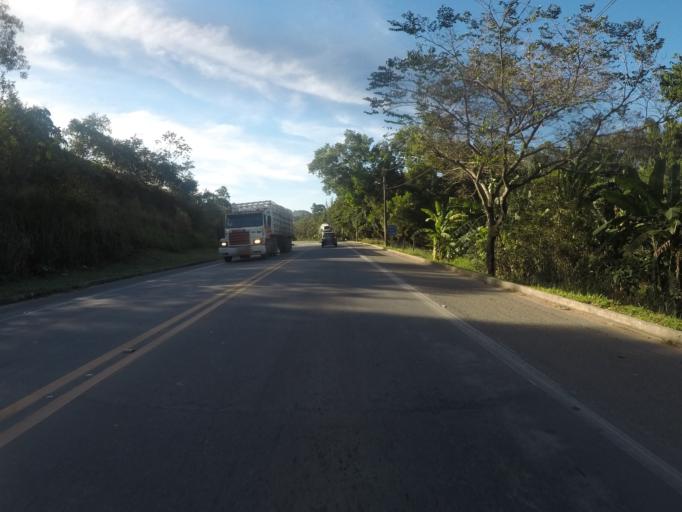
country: BR
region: Espirito Santo
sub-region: Fundao
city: Fundao
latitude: -19.9294
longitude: -40.4061
